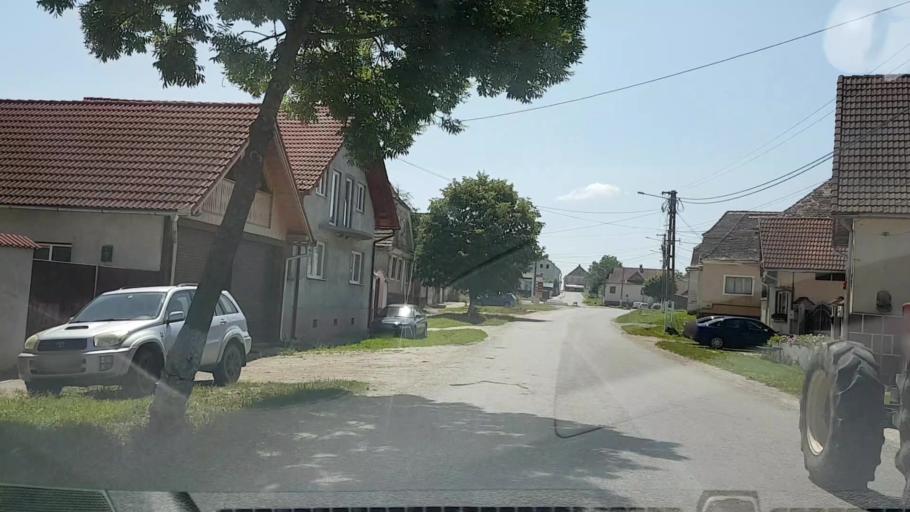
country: RO
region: Brasov
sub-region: Comuna Cincu
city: Cincu
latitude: 45.9183
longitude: 24.8007
